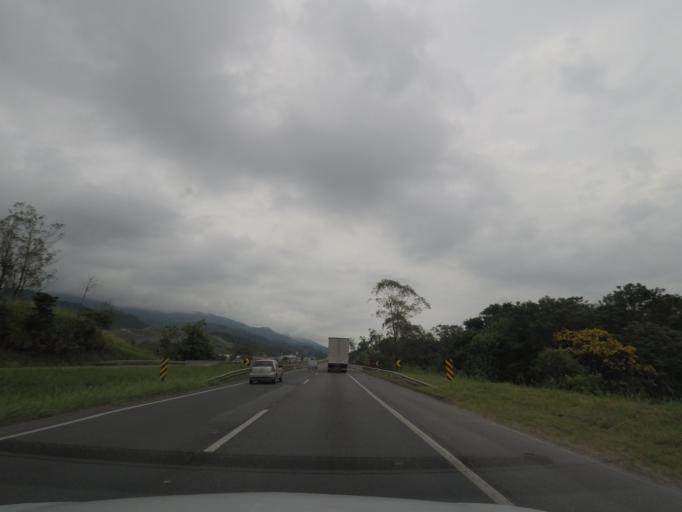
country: BR
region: Sao Paulo
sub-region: Miracatu
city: Miracatu
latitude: -24.2703
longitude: -47.4008
